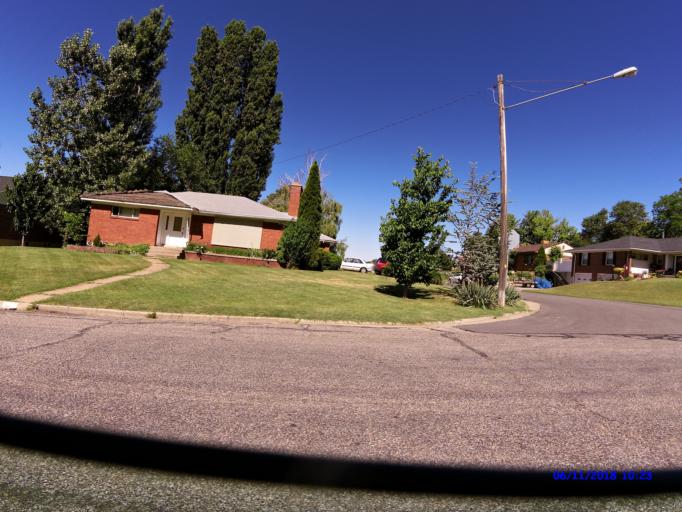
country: US
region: Utah
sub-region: Weber County
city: South Ogden
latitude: 41.2077
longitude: -111.9413
